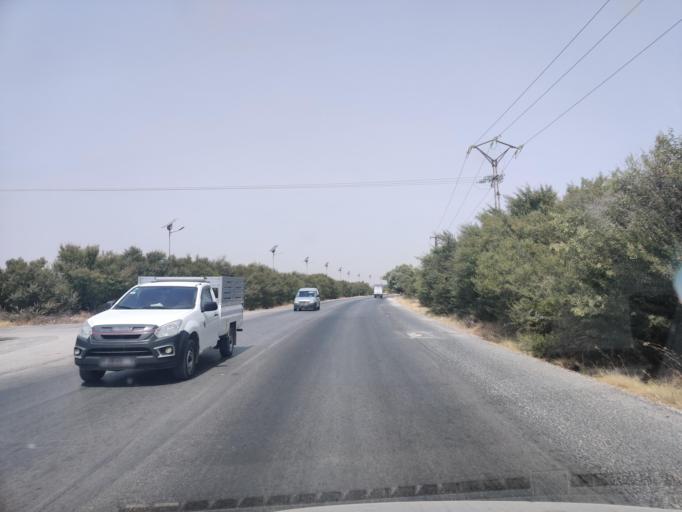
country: TN
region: Tunis
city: La Sebala du Mornag
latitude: 36.6518
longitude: 10.3364
